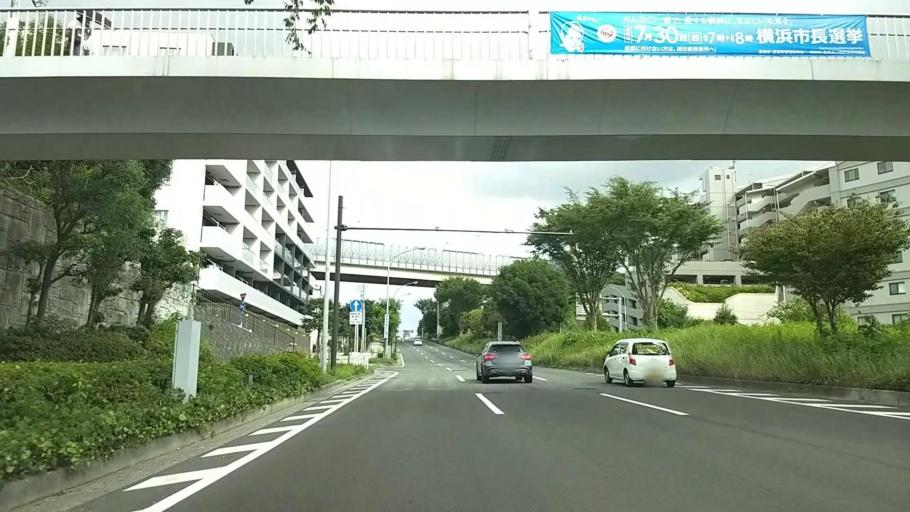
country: JP
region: Kanagawa
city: Yokohama
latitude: 35.4022
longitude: 139.5746
